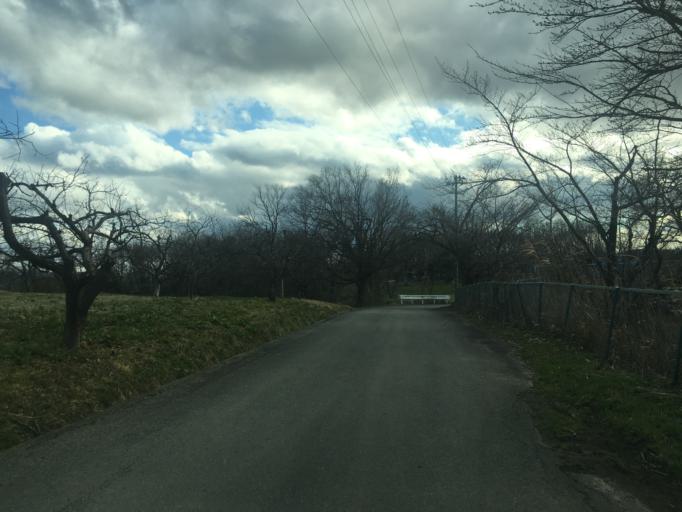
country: JP
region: Fukushima
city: Yanagawamachi-saiwaicho
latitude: 37.8879
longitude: 140.5741
